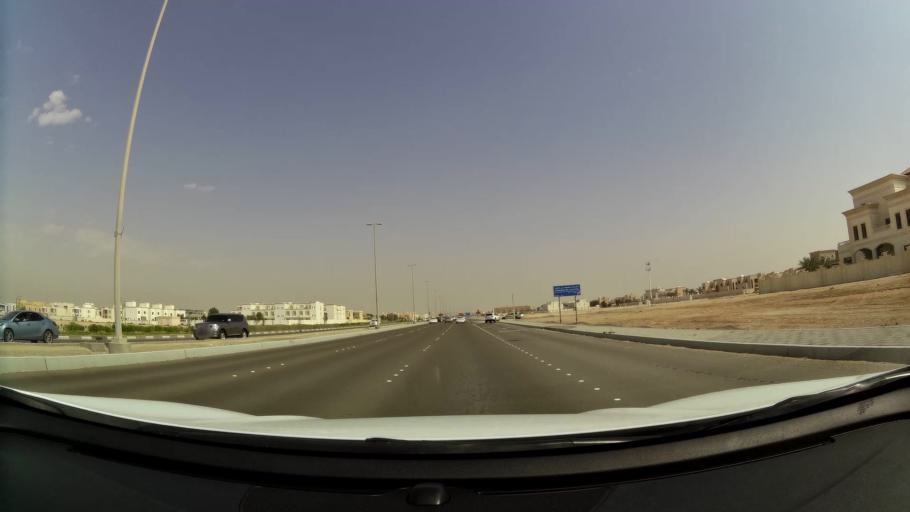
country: AE
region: Abu Dhabi
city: Abu Dhabi
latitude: 24.3475
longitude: 54.5476
